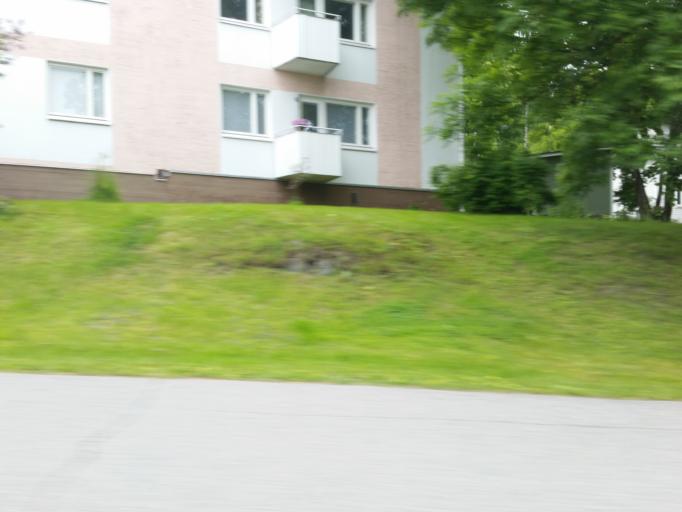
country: FI
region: Northern Savo
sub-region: Kuopio
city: Kuopio
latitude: 62.8857
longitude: 27.6787
